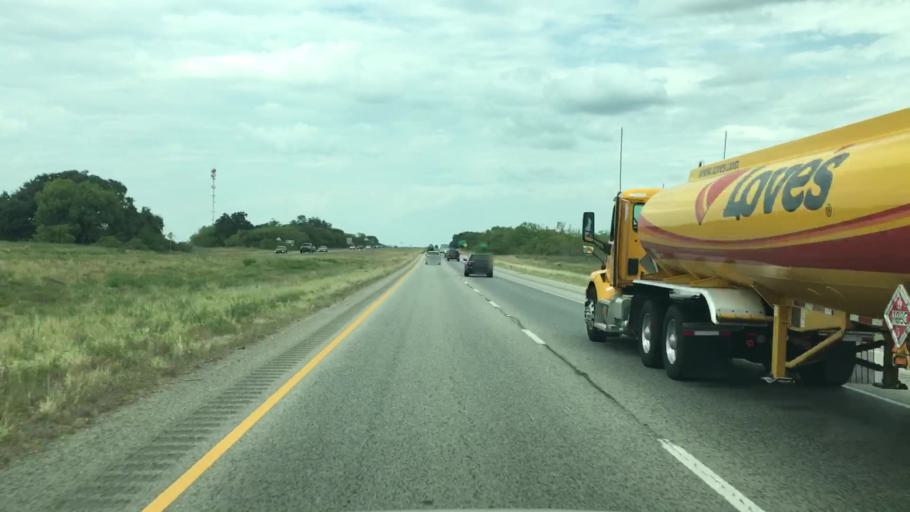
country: US
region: Texas
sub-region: Atascosa County
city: Poteet
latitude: 29.1204
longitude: -98.4312
